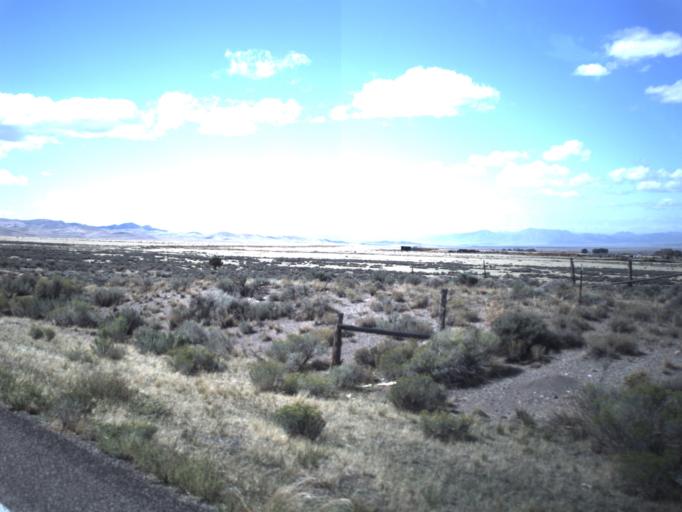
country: US
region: Utah
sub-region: Beaver County
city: Milford
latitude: 38.2017
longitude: -112.9307
